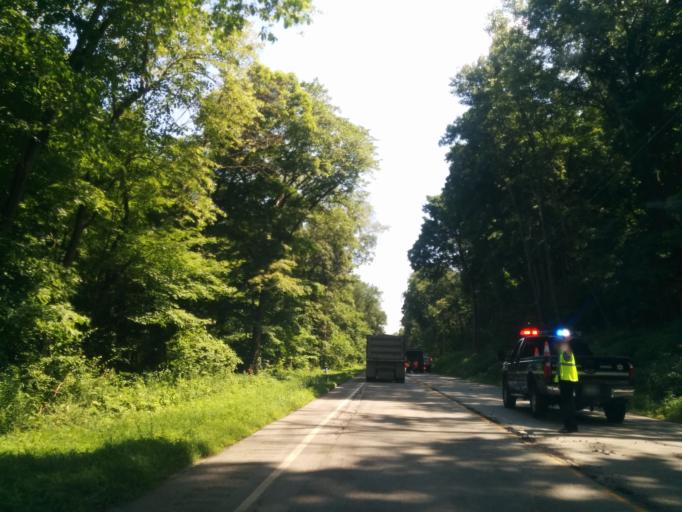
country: US
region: Illinois
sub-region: Cook County
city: Willow Springs
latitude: 41.7192
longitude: -87.8916
